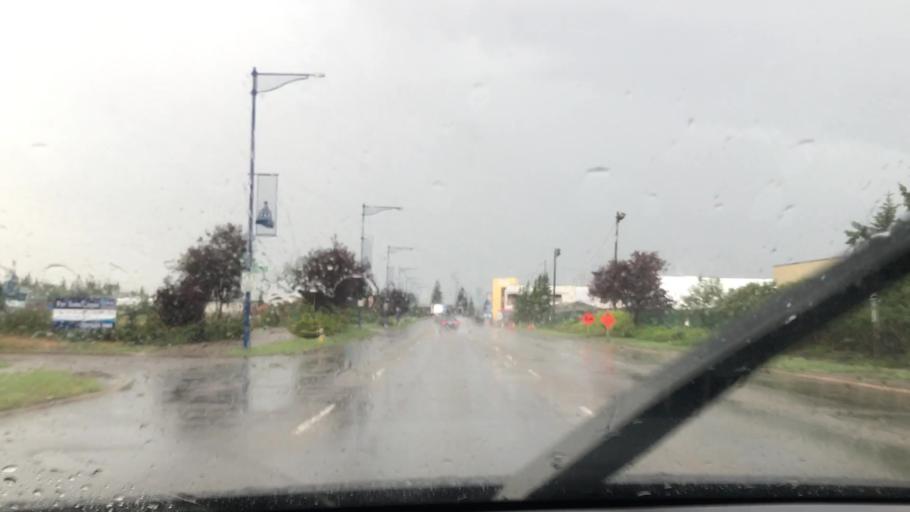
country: CA
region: Alberta
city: Edmonton
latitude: 53.5042
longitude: -113.4947
